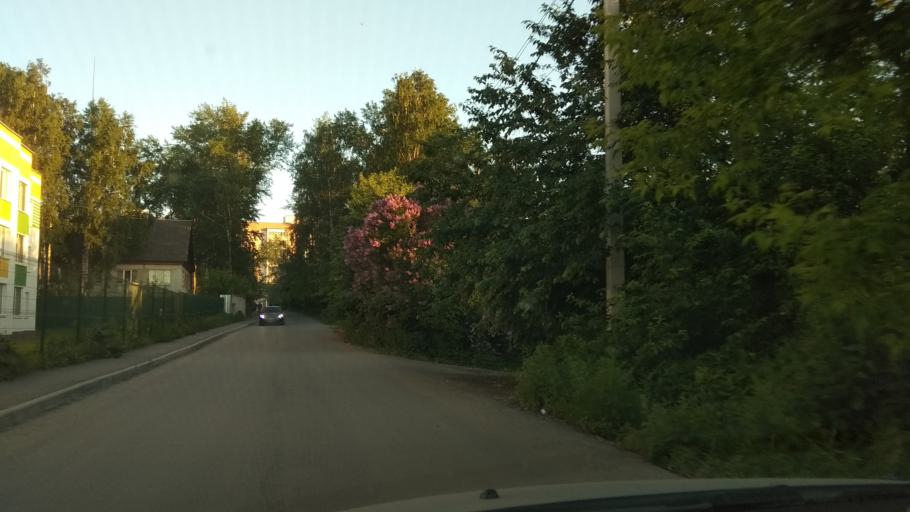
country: RU
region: Sverdlovsk
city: Sredneuralsk
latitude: 56.9909
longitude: 60.4576
